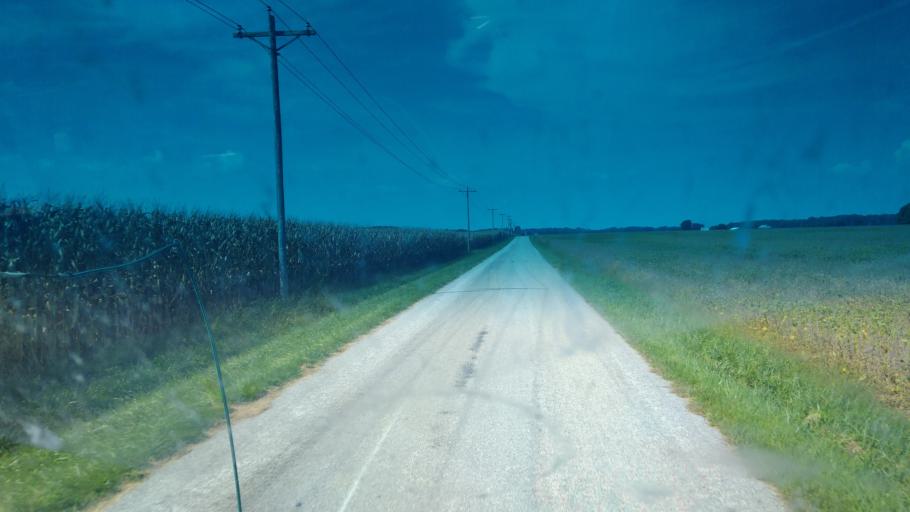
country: US
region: Ohio
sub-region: Wyandot County
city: Upper Sandusky
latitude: 40.6585
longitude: -83.2827
